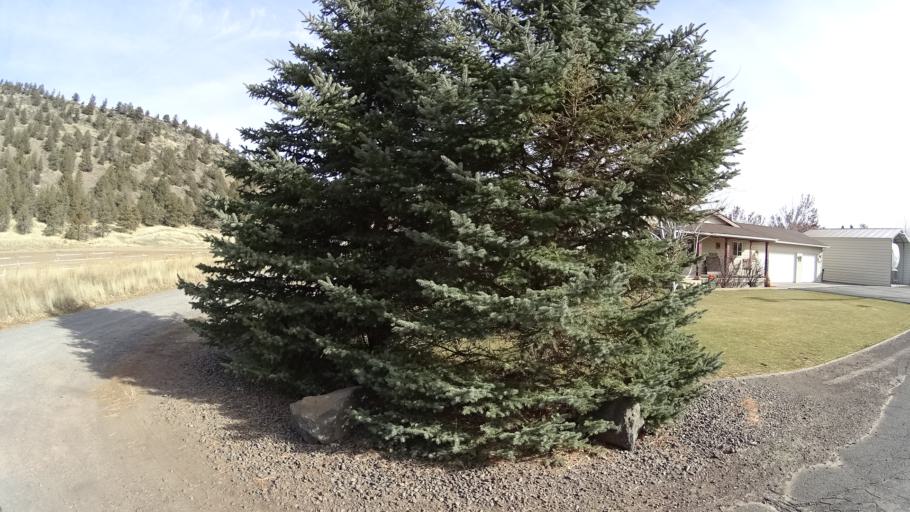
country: US
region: Oregon
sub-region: Klamath County
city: Klamath Falls
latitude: 41.9713
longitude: -121.9161
